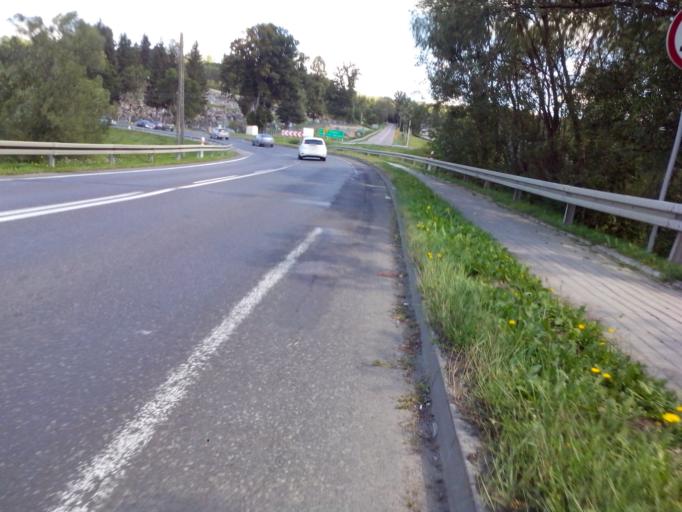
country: PL
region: Subcarpathian Voivodeship
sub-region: Powiat brzozowski
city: Domaradz
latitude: 49.7932
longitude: 21.9478
